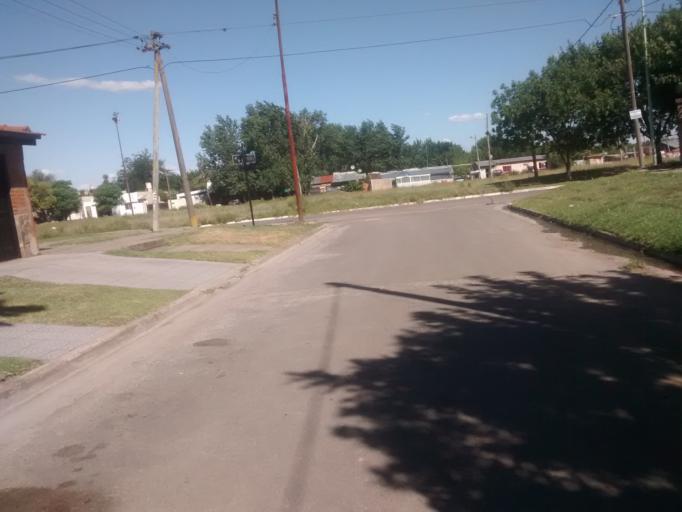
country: AR
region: Buenos Aires
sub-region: Partido de La Plata
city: La Plata
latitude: -34.9353
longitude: -57.9020
